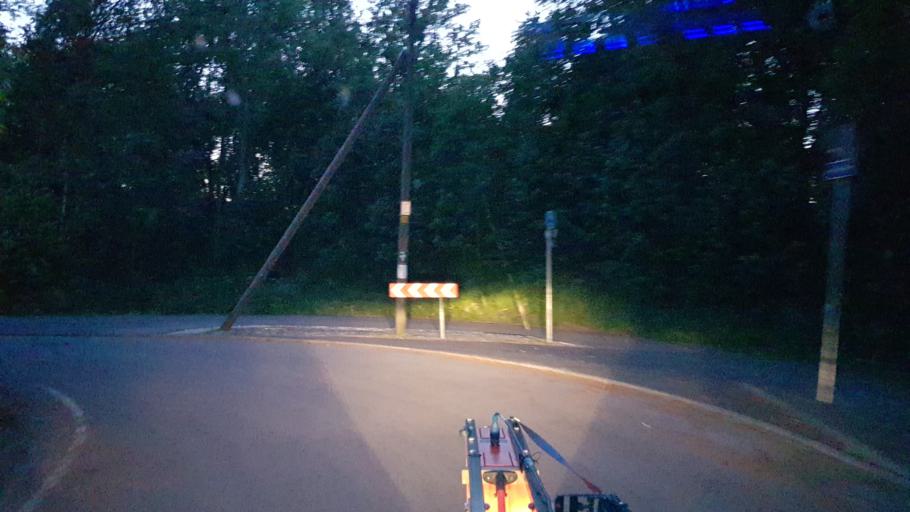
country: EE
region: Harju
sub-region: Harku vald
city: Tabasalu
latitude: 59.4605
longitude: 24.5722
